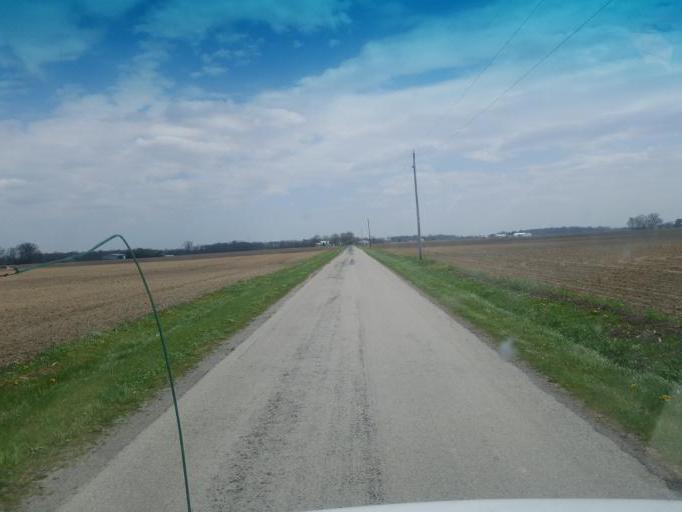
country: US
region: Ohio
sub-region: Wyandot County
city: Upper Sandusky
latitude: 40.7741
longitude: -83.3328
